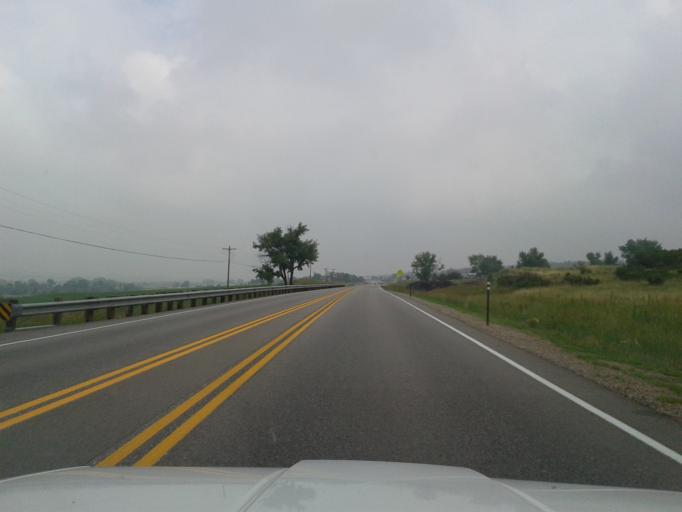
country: US
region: Colorado
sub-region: Douglas County
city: The Pinery
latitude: 39.3798
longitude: -104.7507
